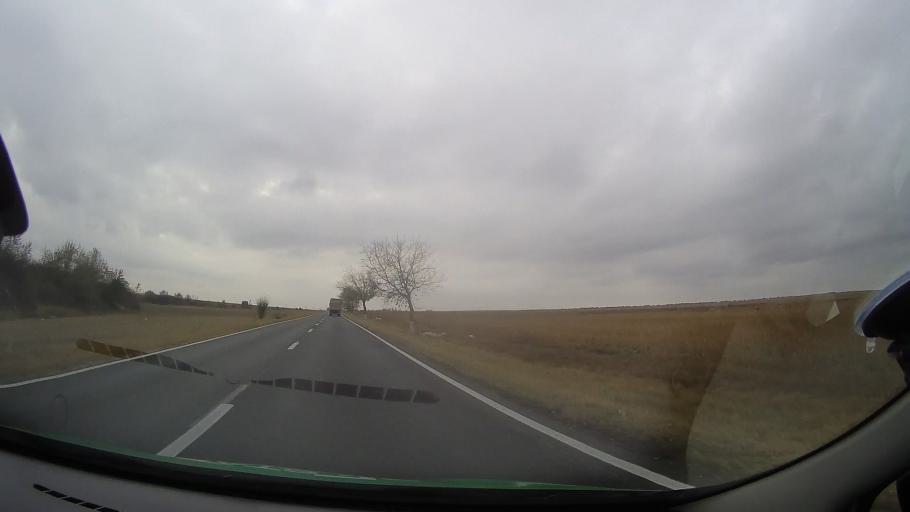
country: RO
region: Constanta
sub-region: Comuna Castelu
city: Castelu
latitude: 44.2536
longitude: 28.3162
